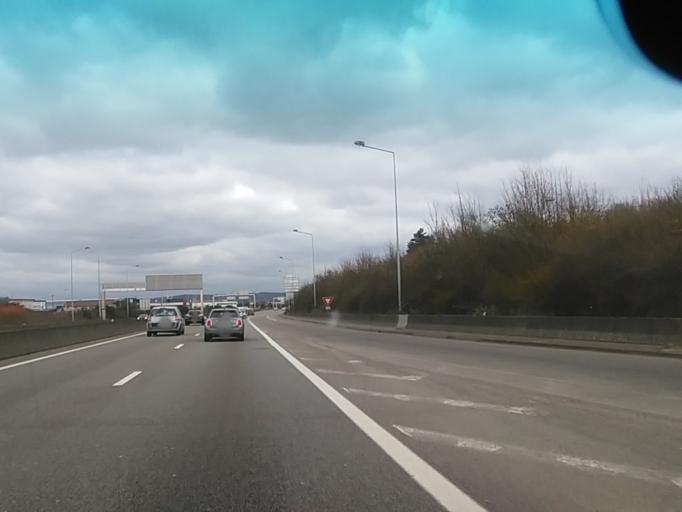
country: FR
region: Haute-Normandie
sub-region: Departement de la Seine-Maritime
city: Le Grand-Quevilly
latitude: 49.4020
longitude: 1.0331
